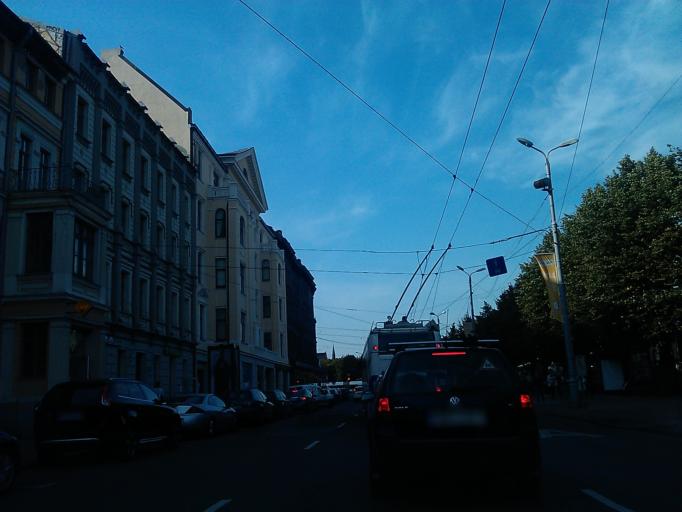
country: LV
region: Riga
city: Riga
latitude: 56.9513
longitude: 24.1166
